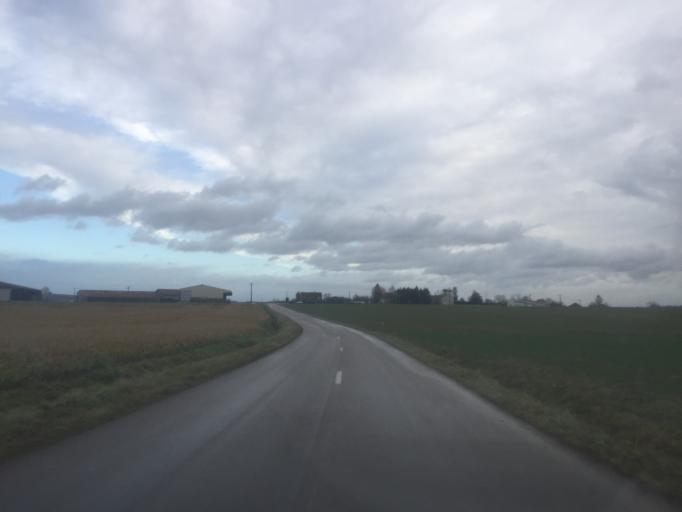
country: FR
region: Franche-Comte
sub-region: Departement de la Haute-Saone
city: Pesmes
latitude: 47.2431
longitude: 5.6021
